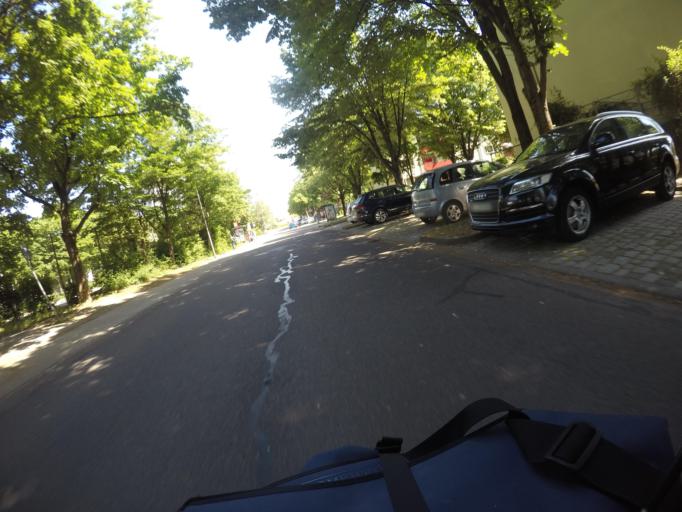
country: DE
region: Baden-Wuerttemberg
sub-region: Karlsruhe Region
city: Karlsruhe
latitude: 48.9966
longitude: 8.3538
